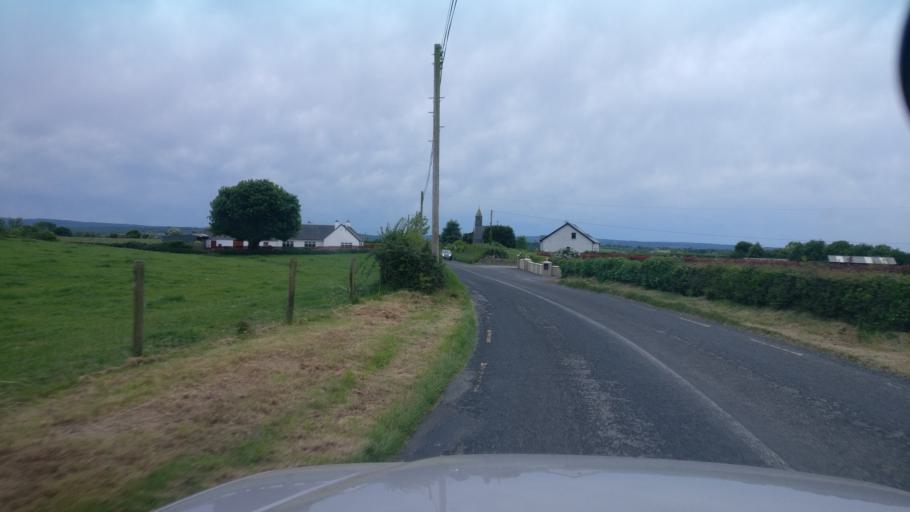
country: IE
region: Connaught
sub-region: County Galway
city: Portumna
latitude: 53.1133
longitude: -8.2797
